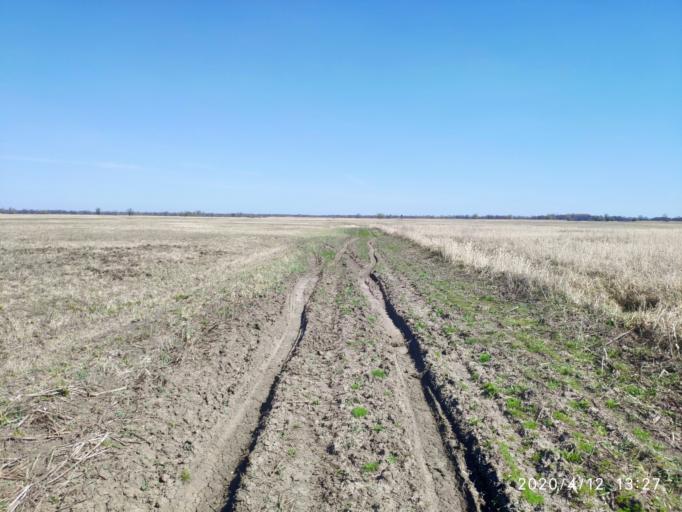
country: PL
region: Lubusz
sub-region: Powiat krosnienski
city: Dabie
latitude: 52.0509
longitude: 15.1956
